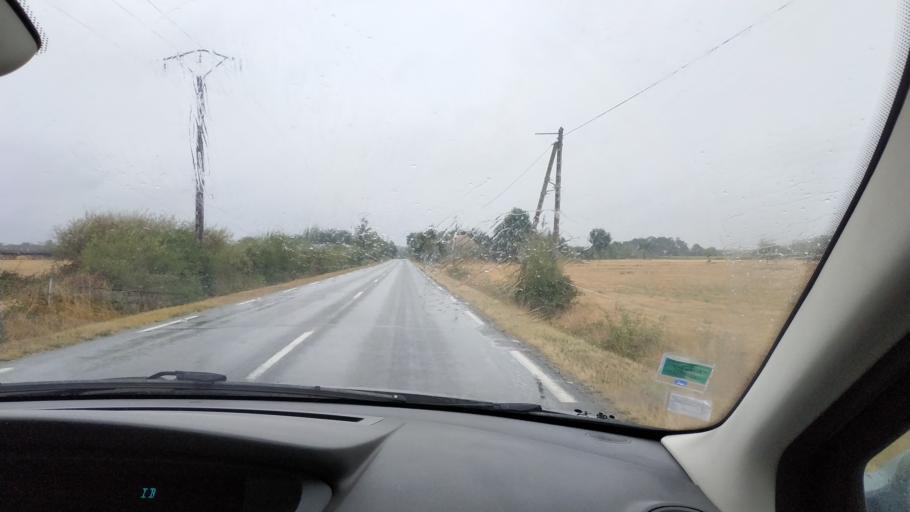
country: FR
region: Centre
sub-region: Departement du Loiret
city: Bellegarde
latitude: 47.9435
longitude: 2.3829
